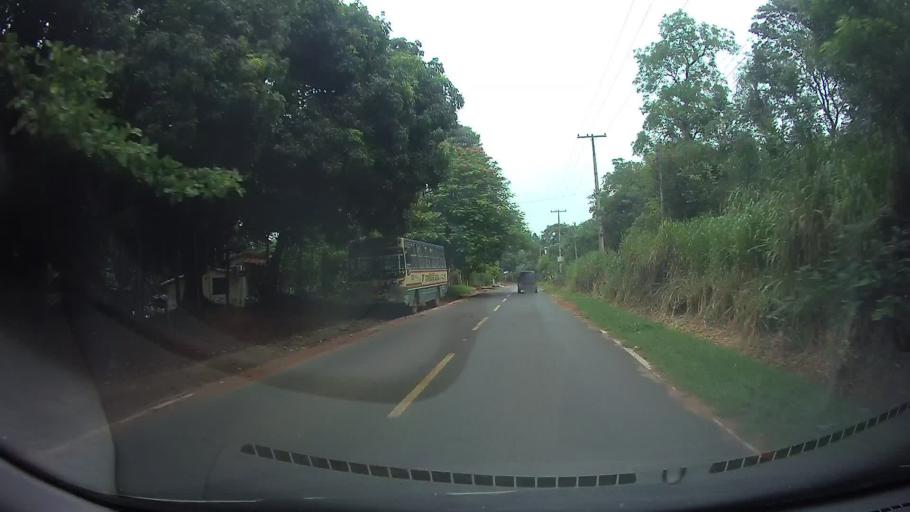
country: PY
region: Central
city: Itaugua
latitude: -25.3568
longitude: -57.3439
